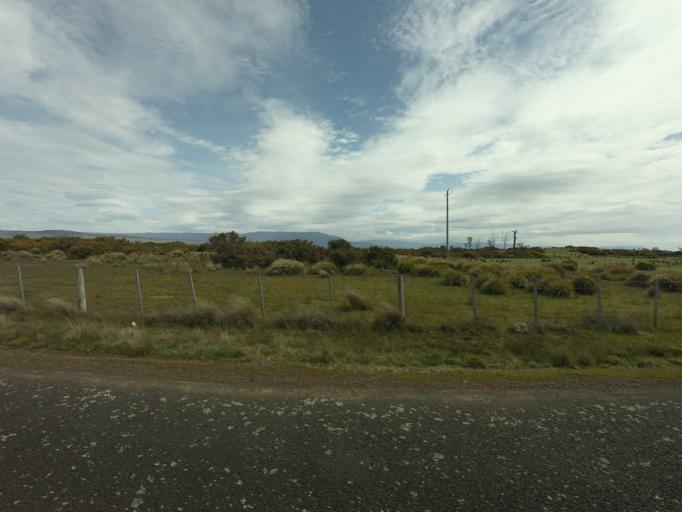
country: AU
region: Tasmania
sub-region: Northern Midlands
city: Evandale
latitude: -41.8349
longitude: 147.3296
